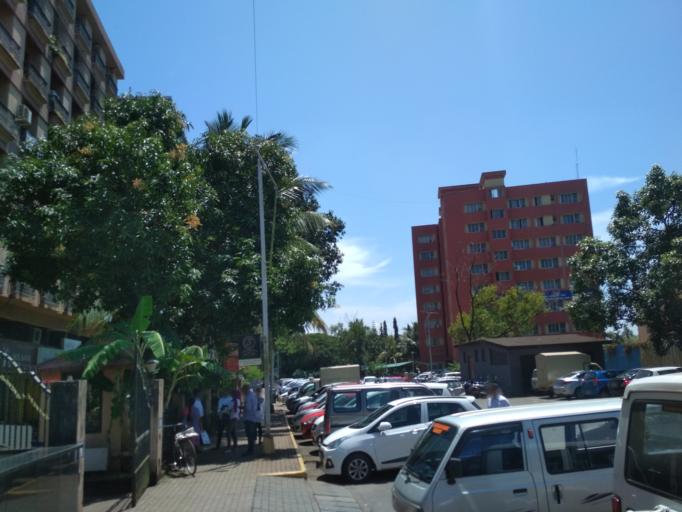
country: IN
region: Goa
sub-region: North Goa
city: Panaji
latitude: 15.4941
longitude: 73.8354
